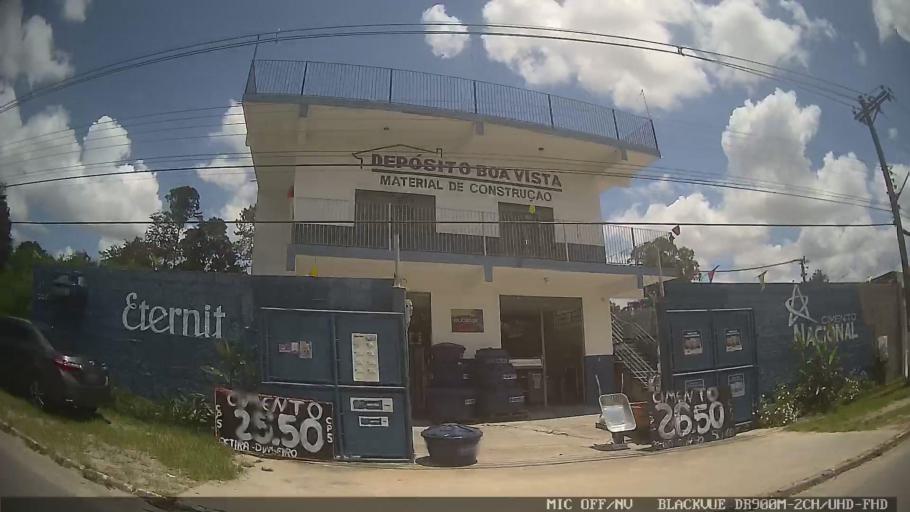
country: BR
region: Sao Paulo
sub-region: Jacarei
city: Jacarei
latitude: -23.3163
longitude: -45.9242
